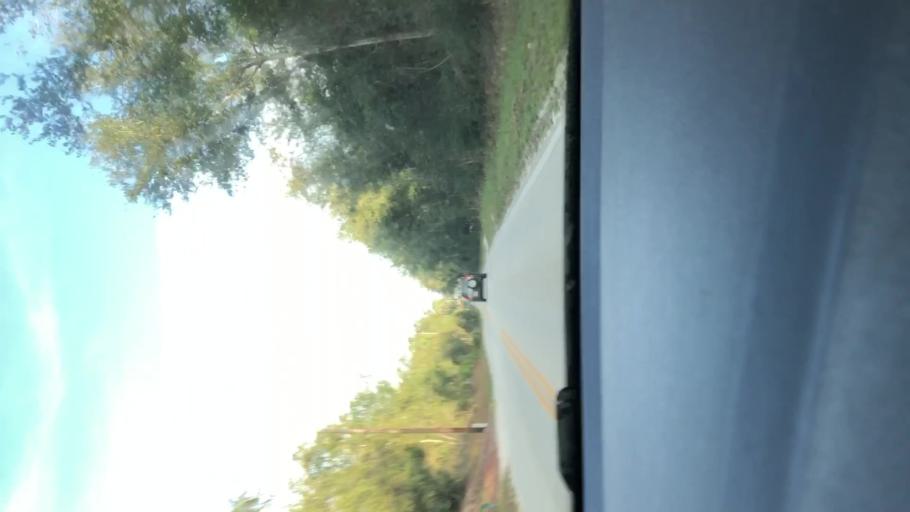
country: US
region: Florida
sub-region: Volusia County
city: Orange City
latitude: 28.9524
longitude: -81.3281
